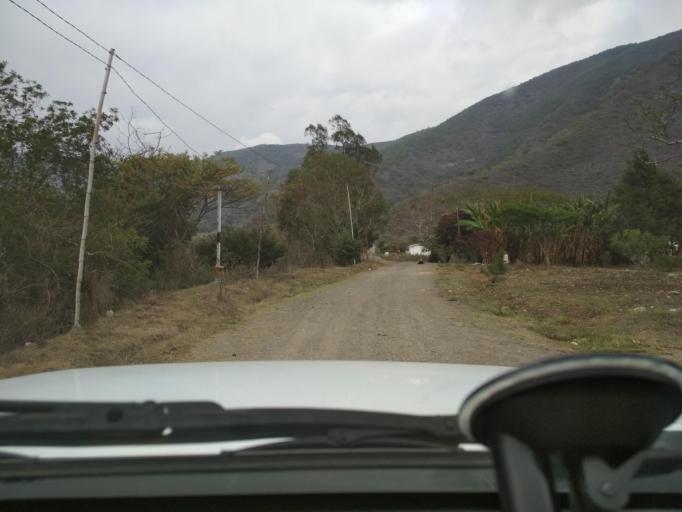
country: MX
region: Veracruz
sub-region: Nogales
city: Taza de Agua Ojo Zarco
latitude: 18.7892
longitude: -97.2148
